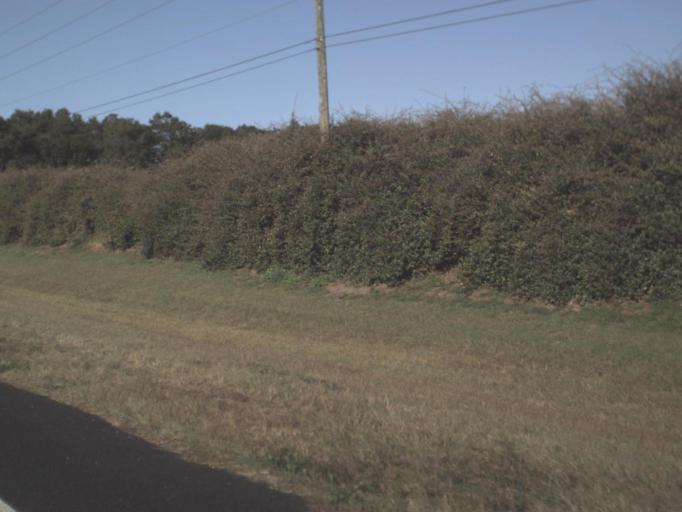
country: US
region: Florida
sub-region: Marion County
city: Belleview
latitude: 29.0258
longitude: -82.1345
